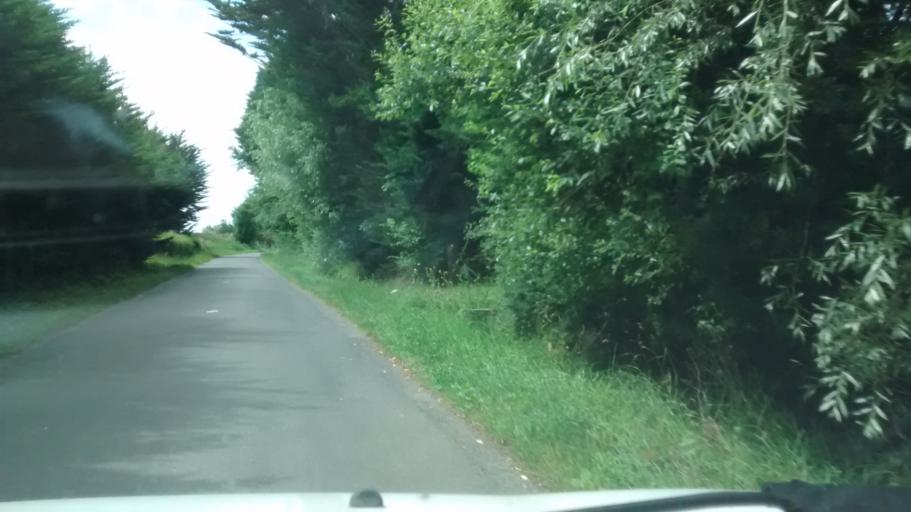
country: FR
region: Brittany
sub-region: Departement d'Ille-et-Vilaine
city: La Gouesniere
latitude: 48.6159
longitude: -1.8653
